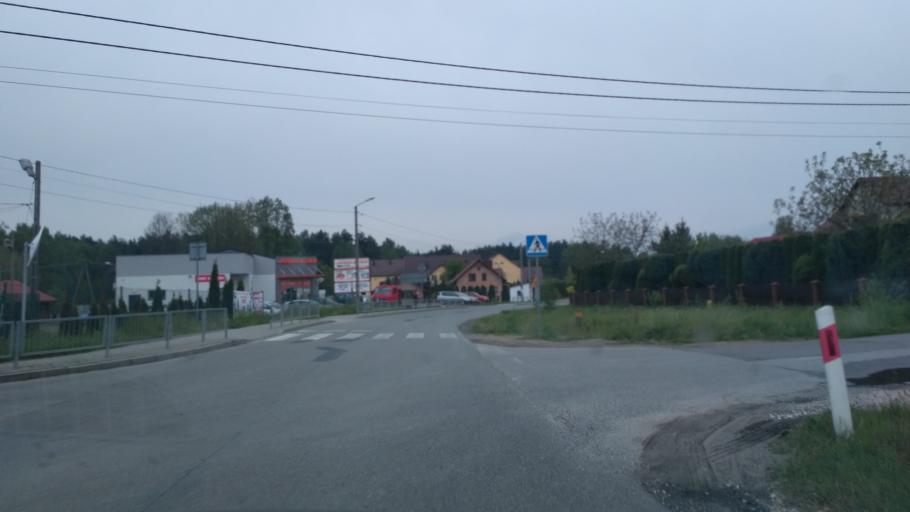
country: PL
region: Subcarpathian Voivodeship
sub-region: Powiat ropczycko-sedziszowski
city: Sedziszow Malopolski
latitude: 50.1251
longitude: 21.7539
